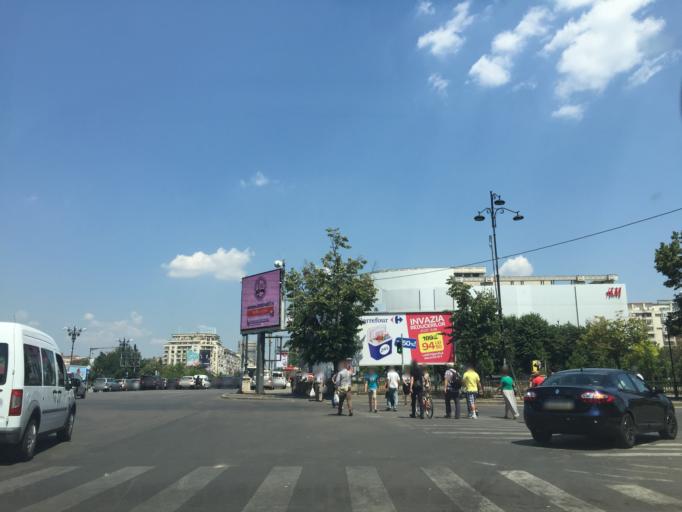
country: RO
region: Bucuresti
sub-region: Municipiul Bucuresti
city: Bucharest
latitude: 44.4255
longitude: 26.1042
